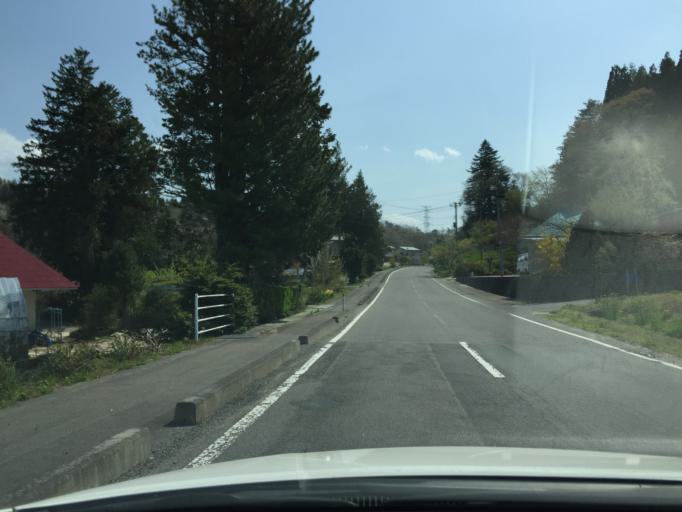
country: JP
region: Fukushima
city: Funehikimachi-funehiki
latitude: 37.4273
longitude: 140.7912
